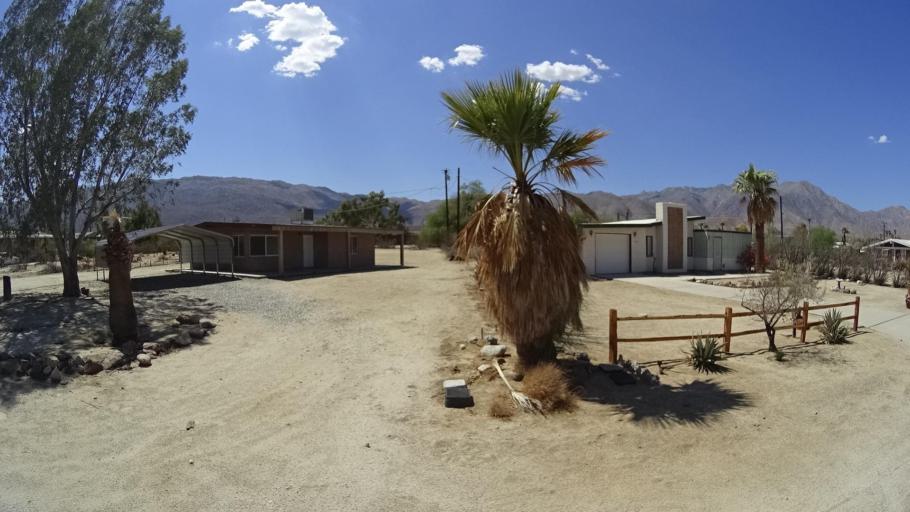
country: US
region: California
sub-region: San Diego County
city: Borrego Springs
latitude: 33.2250
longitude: -116.3701
